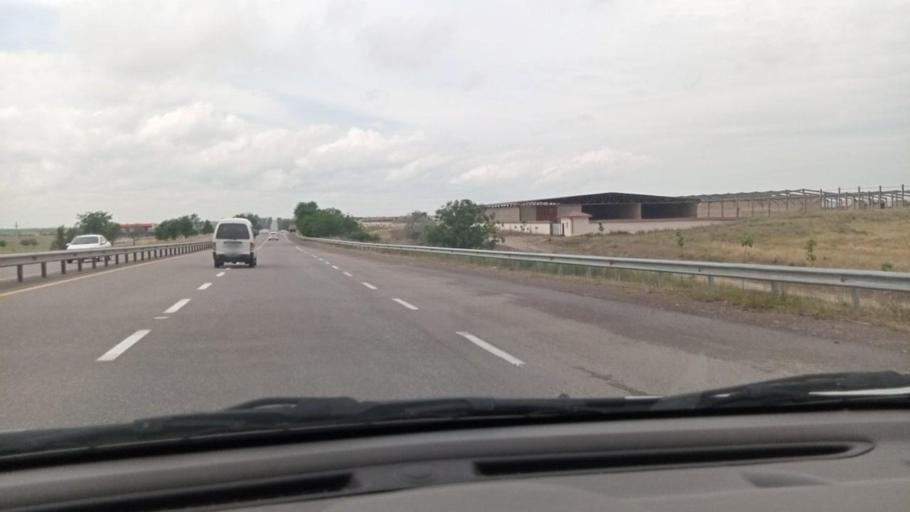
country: UZ
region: Toshkent
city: Ohangaron
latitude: 40.9885
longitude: 69.5346
